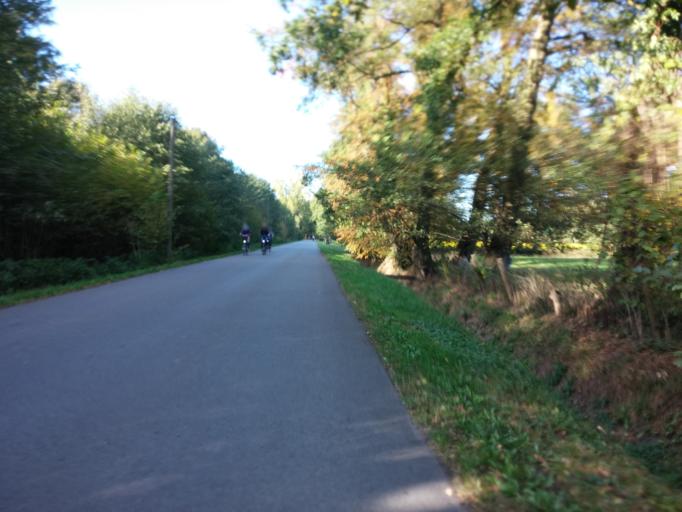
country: DE
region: North Rhine-Westphalia
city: Dorsten
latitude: 51.6367
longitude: 6.9794
